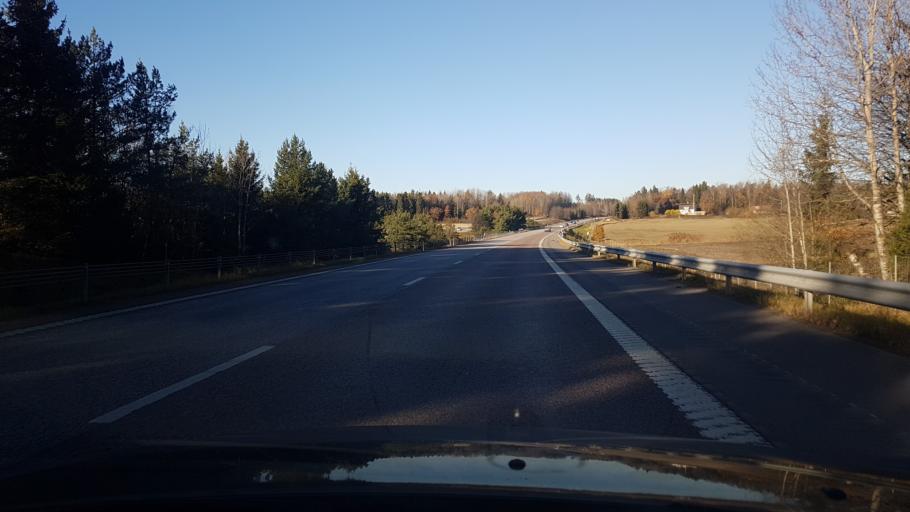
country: SE
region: Uppsala
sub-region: Uppsala Kommun
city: Alsike
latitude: 59.7761
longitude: 17.7833
